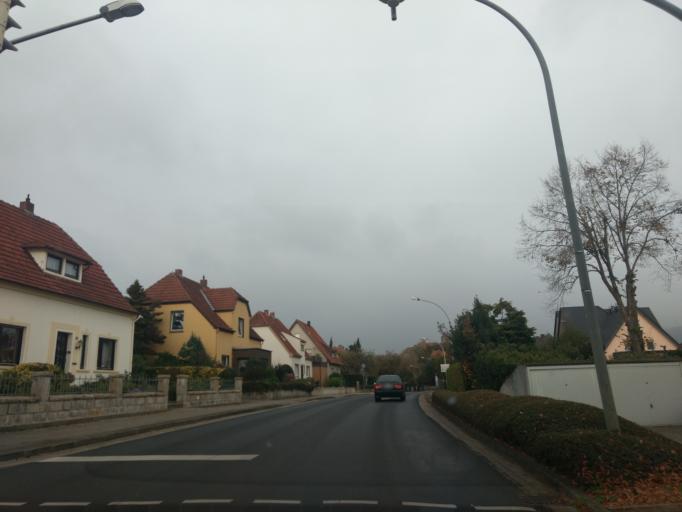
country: DE
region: Lower Saxony
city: Bad Iburg
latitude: 52.1528
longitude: 8.0453
